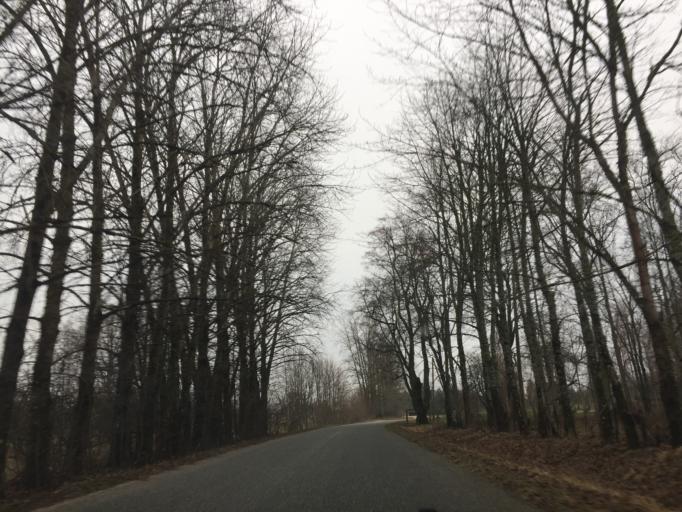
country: LV
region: Limbazu Rajons
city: Limbazi
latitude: 57.6045
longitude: 24.6111
